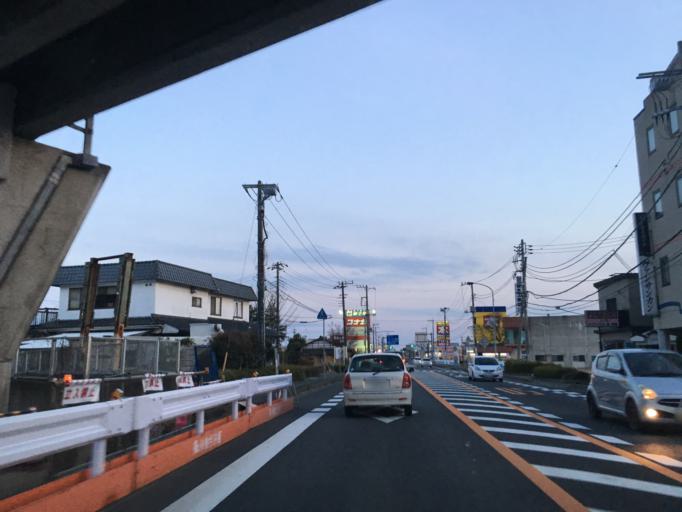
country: JP
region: Ibaraki
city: Takahagi
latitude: 36.7269
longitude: 140.7188
